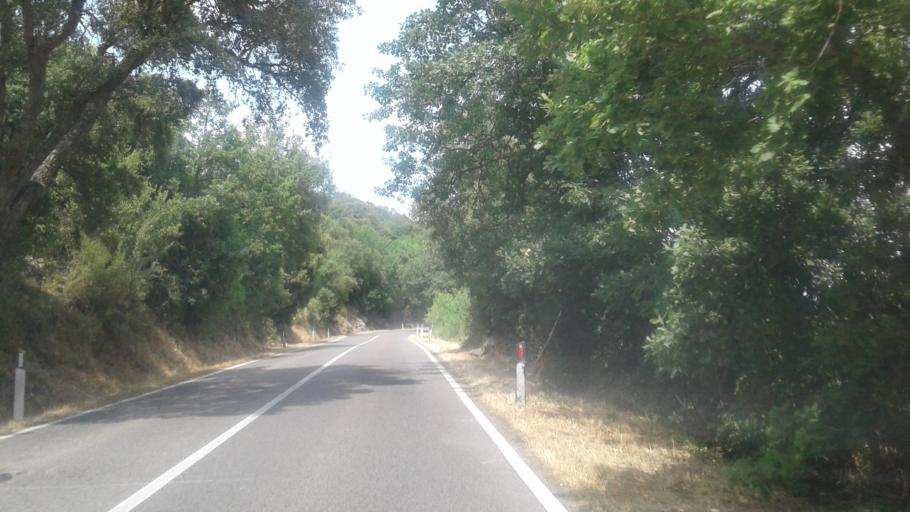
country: IT
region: Sardinia
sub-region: Provincia di Olbia-Tempio
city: Aggius
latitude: 40.9122
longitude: 9.0780
